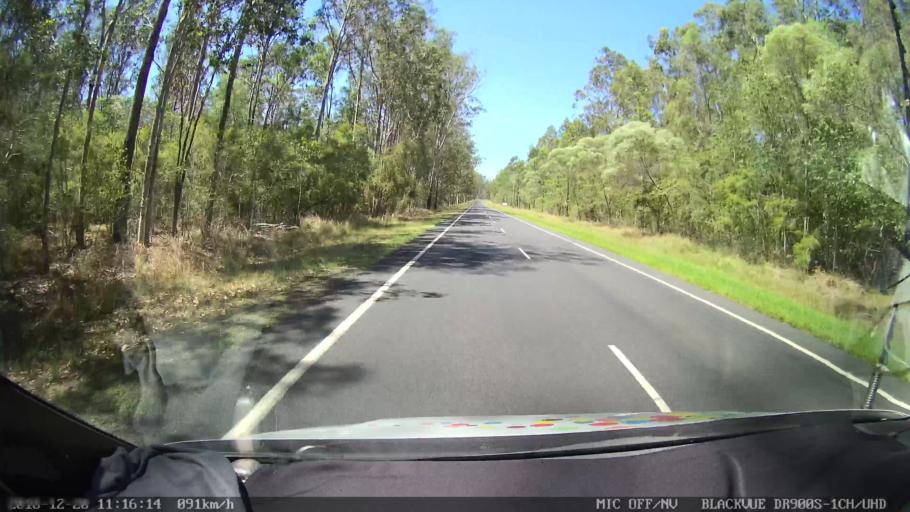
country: AU
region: New South Wales
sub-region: Richmond Valley
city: Casino
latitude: -29.0239
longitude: 153.0107
